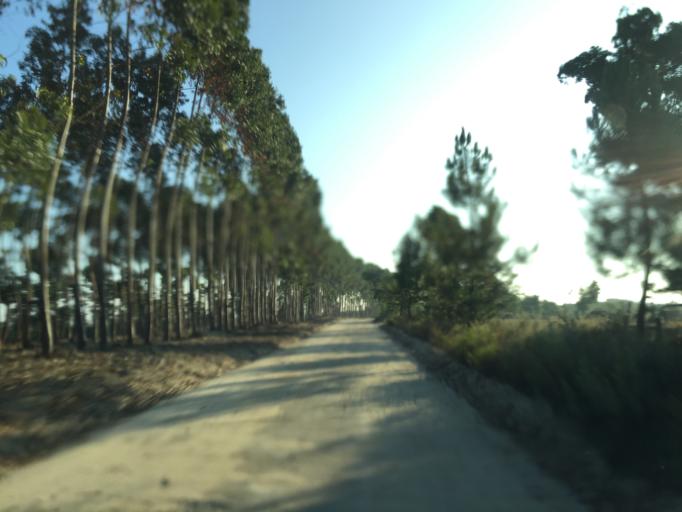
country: PT
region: Portalegre
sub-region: Ponte de Sor
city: Santo Andre
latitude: 39.1206
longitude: -8.3295
